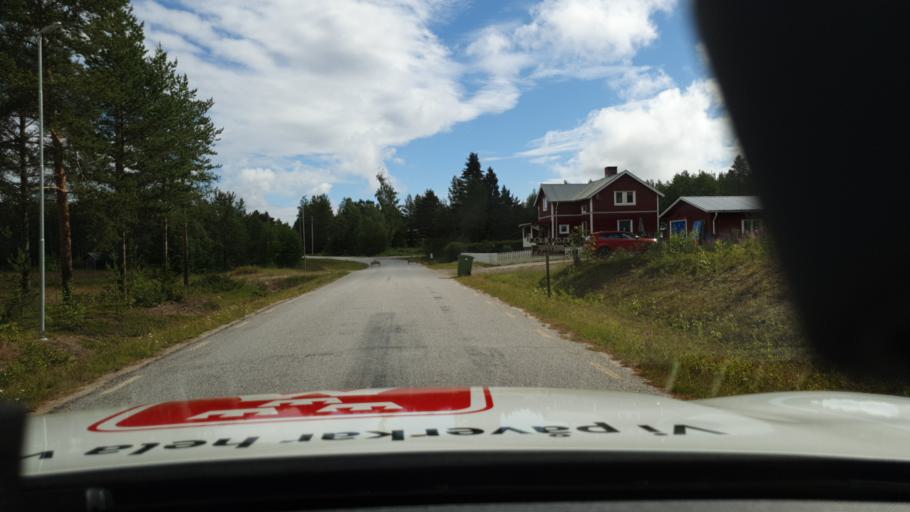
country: SE
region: Norrbotten
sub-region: Pitea Kommun
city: Rosvik
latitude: 65.3892
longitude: 21.7263
